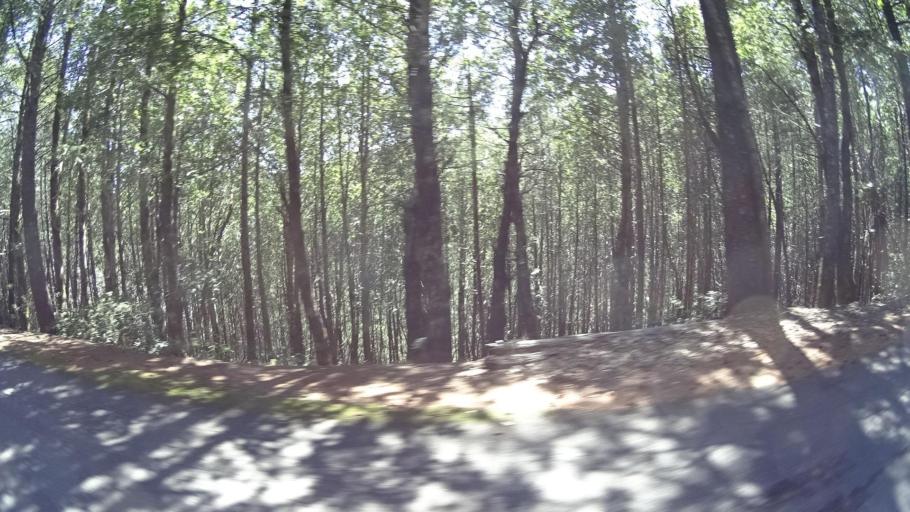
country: US
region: California
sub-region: Humboldt County
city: Redway
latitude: 40.2010
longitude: -124.1011
